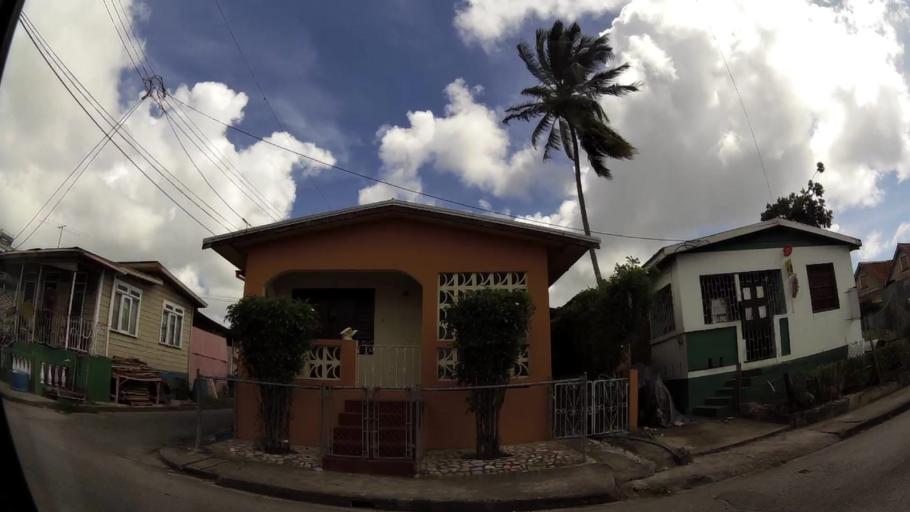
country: BB
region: Saint Michael
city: Bridgetown
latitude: 13.1063
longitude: -59.6171
